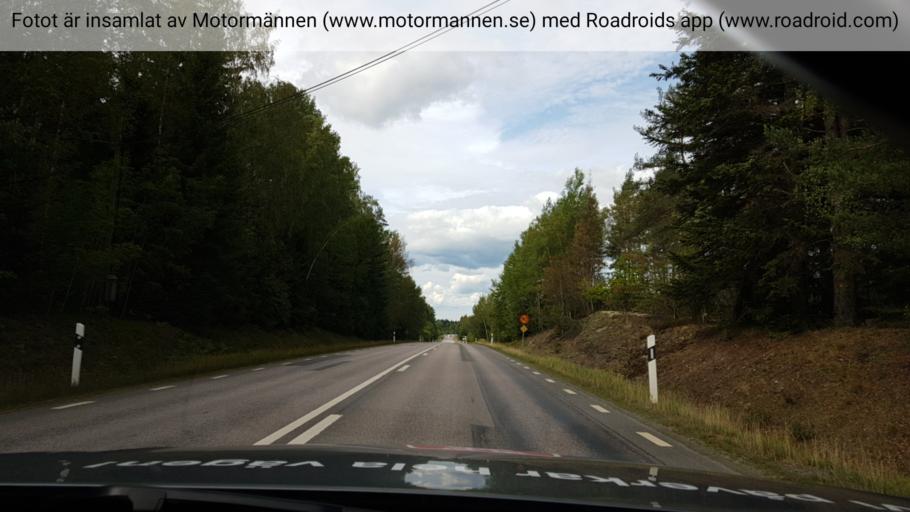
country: SE
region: Uppsala
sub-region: Heby Kommun
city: Morgongava
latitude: 59.8970
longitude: 17.1080
